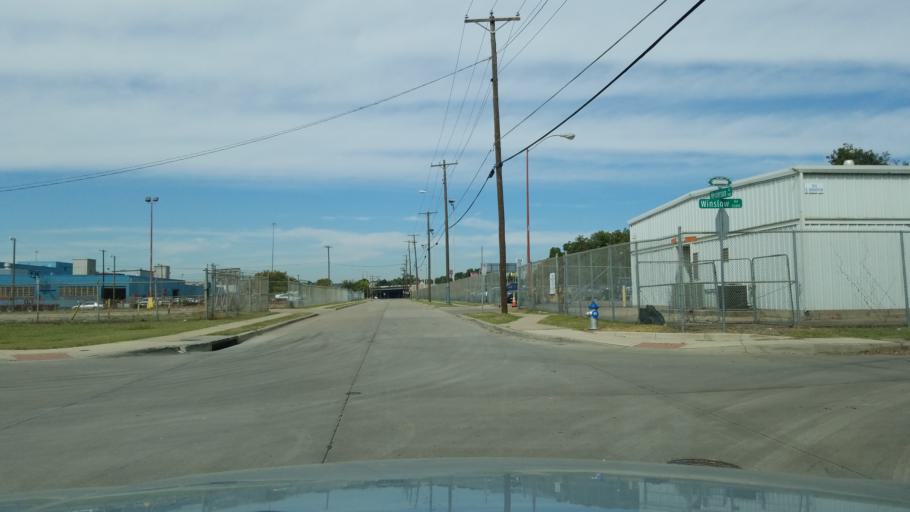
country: US
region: Texas
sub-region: Dallas County
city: Dallas
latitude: 32.7884
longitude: -96.7472
